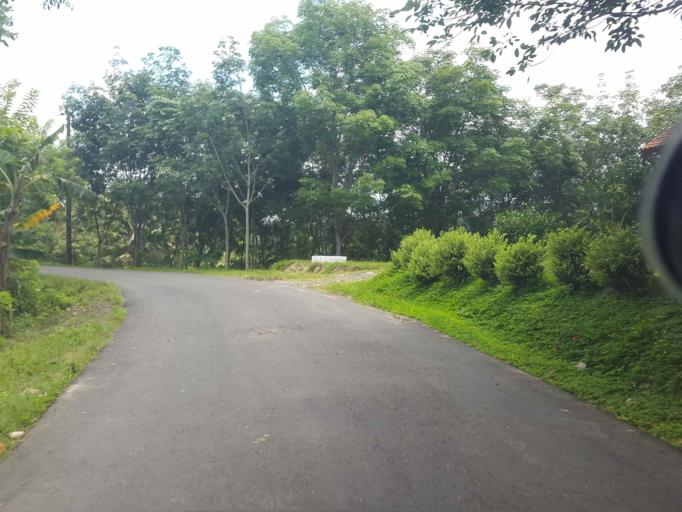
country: ID
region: Central Java
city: Karanggintung
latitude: -7.4476
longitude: 108.9223
